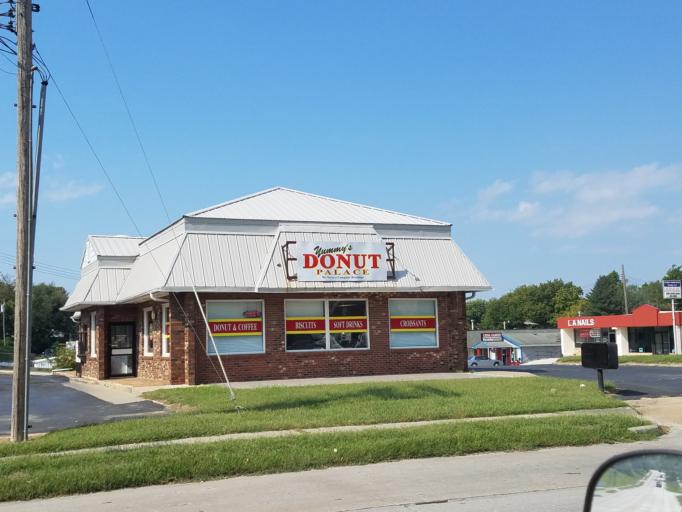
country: US
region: Missouri
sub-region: Cooper County
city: Boonville
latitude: 38.9677
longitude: -92.7413
